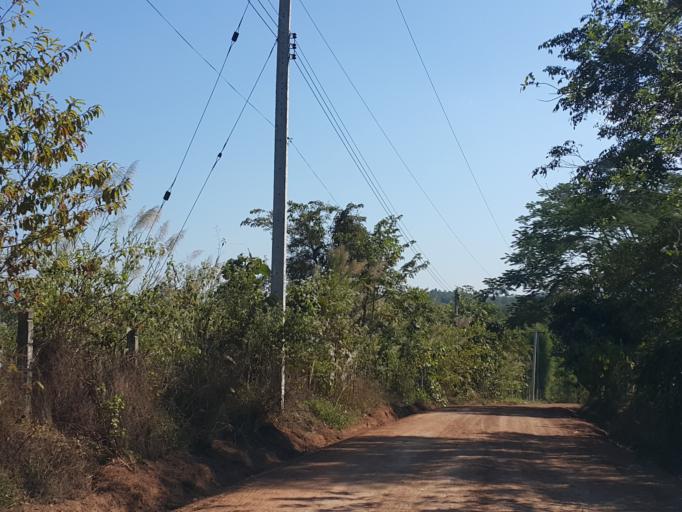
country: TH
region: Chiang Mai
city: Mae Taeng
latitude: 18.9496
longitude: 98.9076
